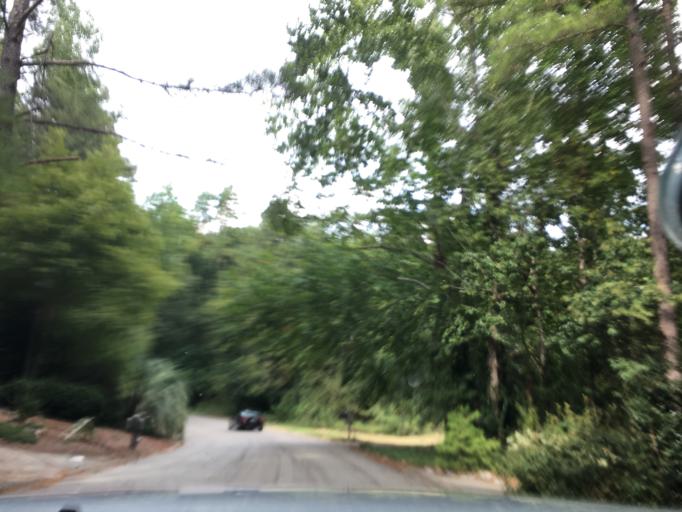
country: US
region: South Carolina
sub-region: Lexington County
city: Irmo
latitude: 34.0579
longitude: -81.1867
